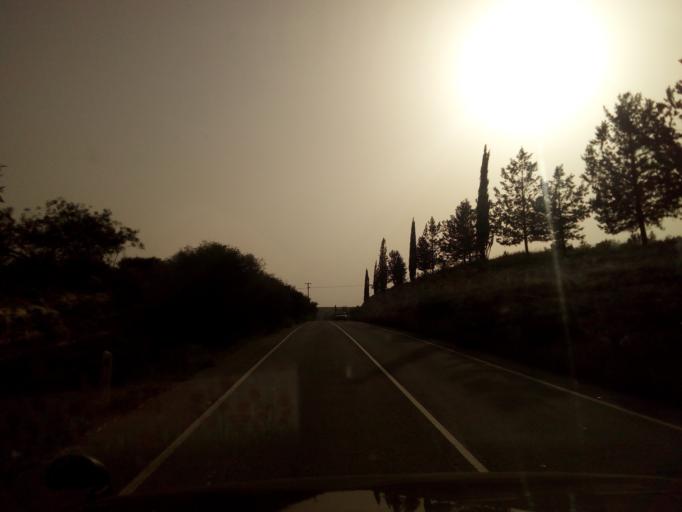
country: CY
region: Lefkosia
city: Lympia
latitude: 34.9985
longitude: 33.4892
